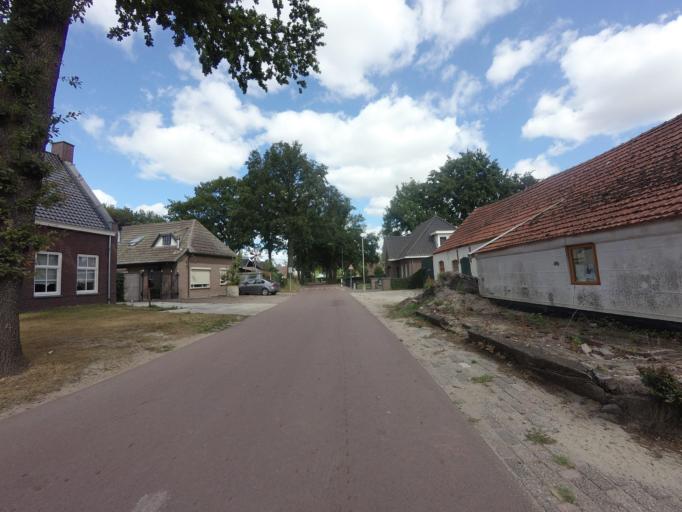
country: NL
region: North Brabant
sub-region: Gemeente Oss
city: Berghem
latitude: 51.7772
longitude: 5.5952
